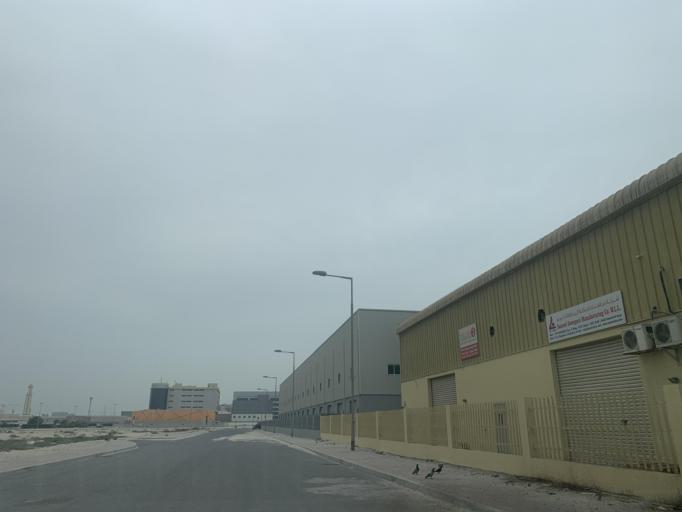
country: BH
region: Muharraq
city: Al Hadd
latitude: 26.2143
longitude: 50.6764
